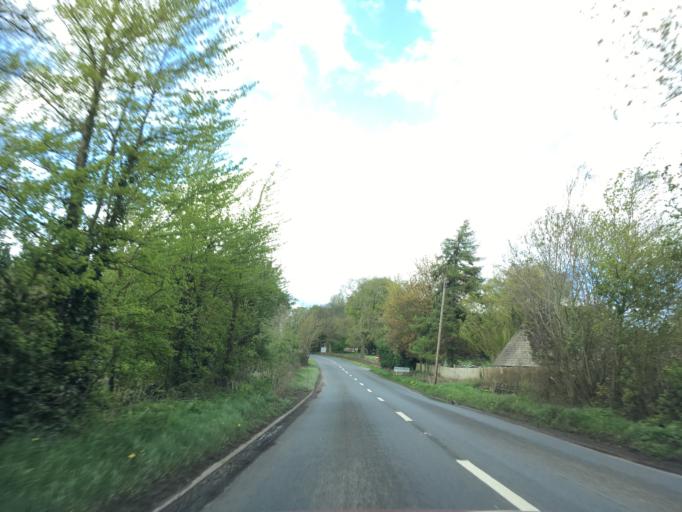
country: GB
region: England
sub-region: Wiltshire
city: Luckington
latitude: 51.6027
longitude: -2.2112
